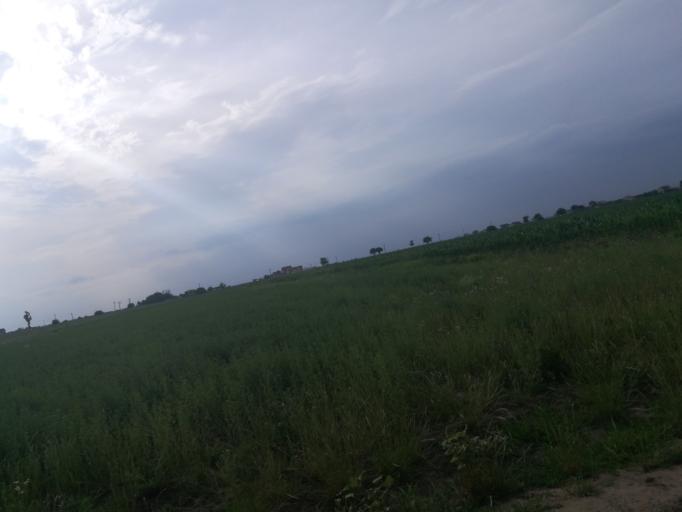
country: RO
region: Ilfov
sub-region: Comuna Vidra
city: Vidra
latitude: 44.2816
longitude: 26.1866
